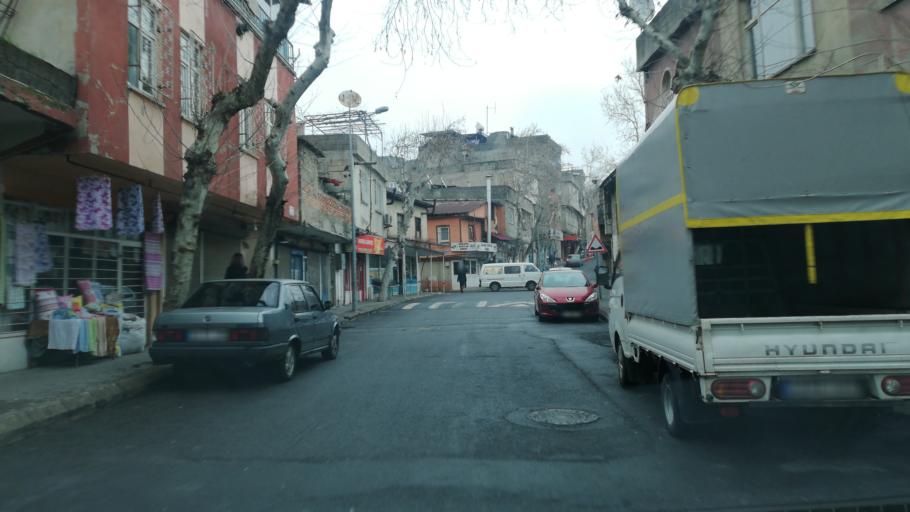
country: TR
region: Kahramanmaras
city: Kahramanmaras
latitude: 37.5813
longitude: 36.9371
